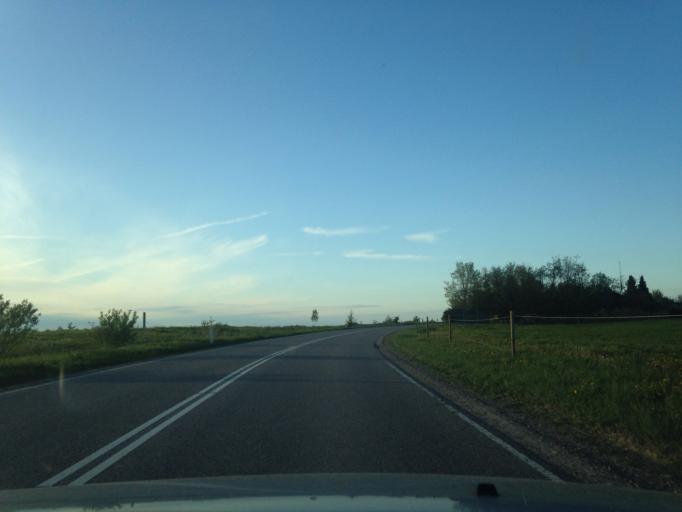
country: DK
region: Zealand
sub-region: Greve Kommune
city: Tune
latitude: 55.6271
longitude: 12.1855
